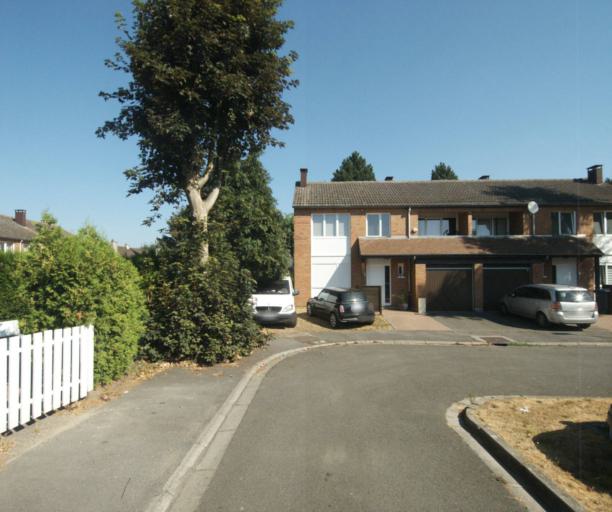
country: FR
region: Nord-Pas-de-Calais
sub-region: Departement du Nord
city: Wervicq-Sud
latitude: 50.7710
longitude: 3.0555
